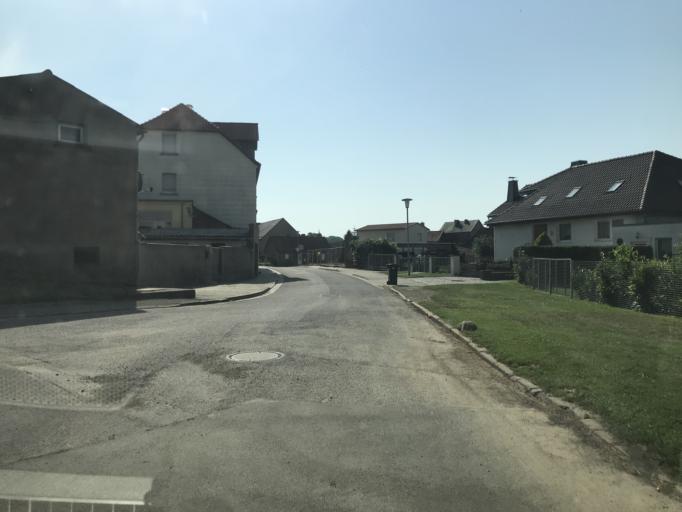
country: DE
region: Saxony-Anhalt
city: Altenhausen
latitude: 52.2551
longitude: 11.2188
